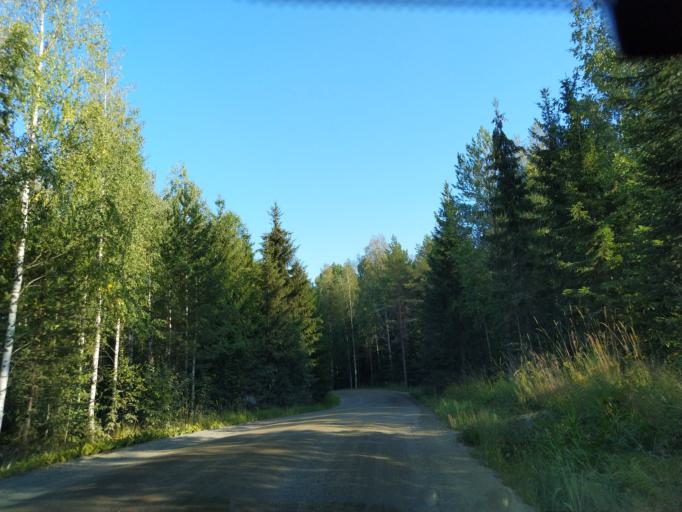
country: FI
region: Central Finland
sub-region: Jaemsae
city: Kuhmoinen
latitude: 61.6176
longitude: 25.1039
